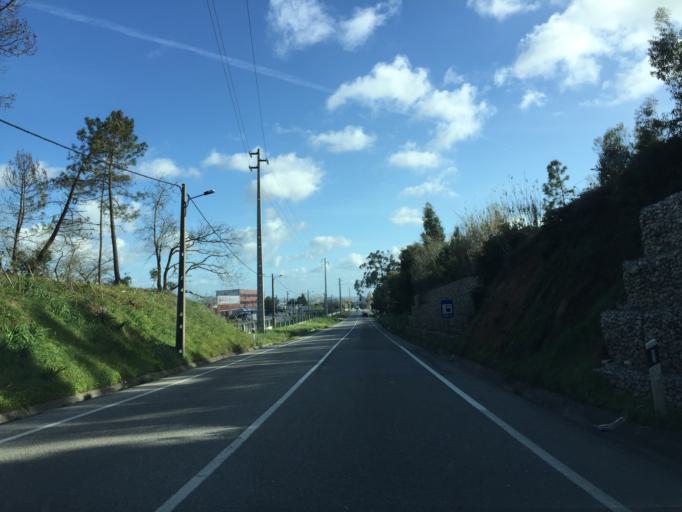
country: PT
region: Coimbra
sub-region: Figueira da Foz
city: Tavarede
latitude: 40.1832
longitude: -8.8292
